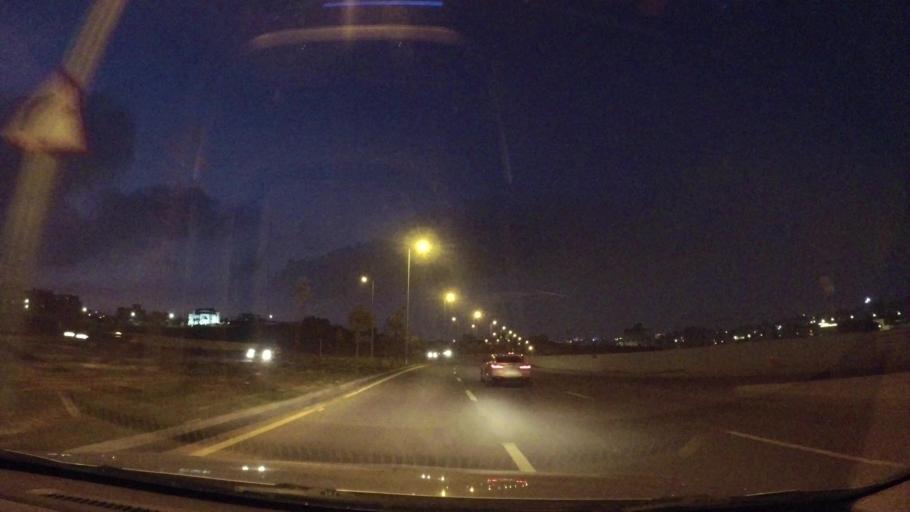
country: JO
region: Amman
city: Al Bunayyat ash Shamaliyah
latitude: 31.9117
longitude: 35.8802
